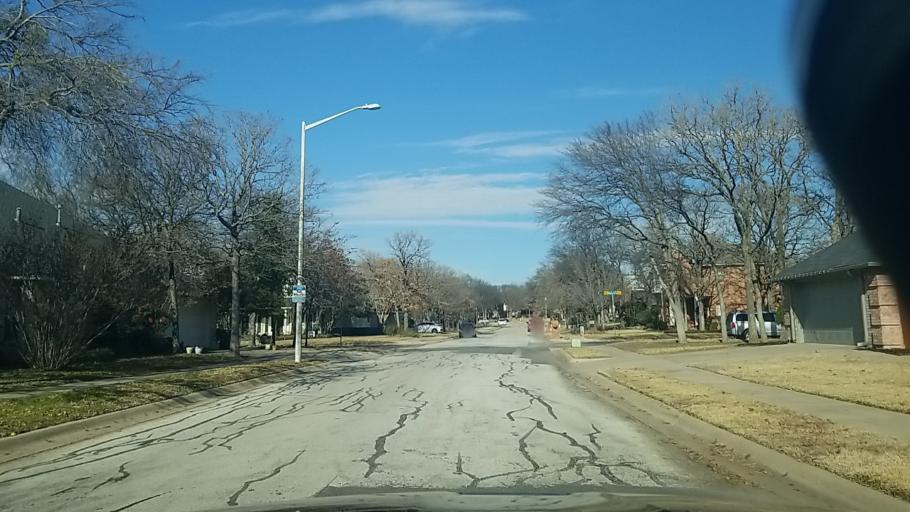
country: US
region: Texas
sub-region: Denton County
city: Corinth
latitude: 33.1481
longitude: -97.1199
